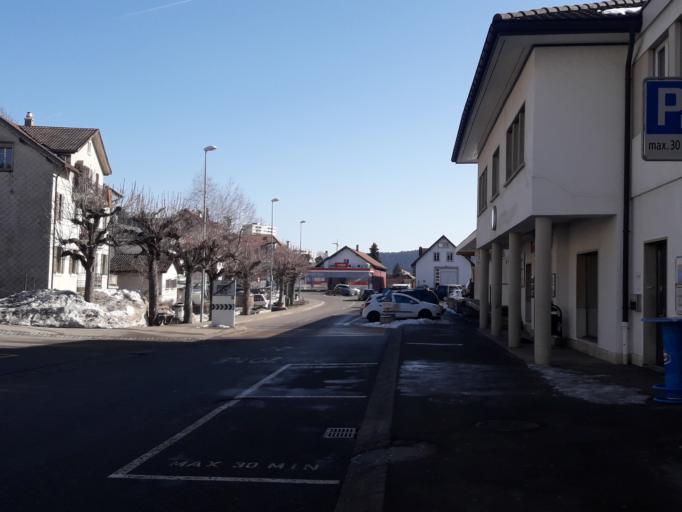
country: CH
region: Bern
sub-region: Jura bernois
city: Tramelan
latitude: 47.2228
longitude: 7.1039
